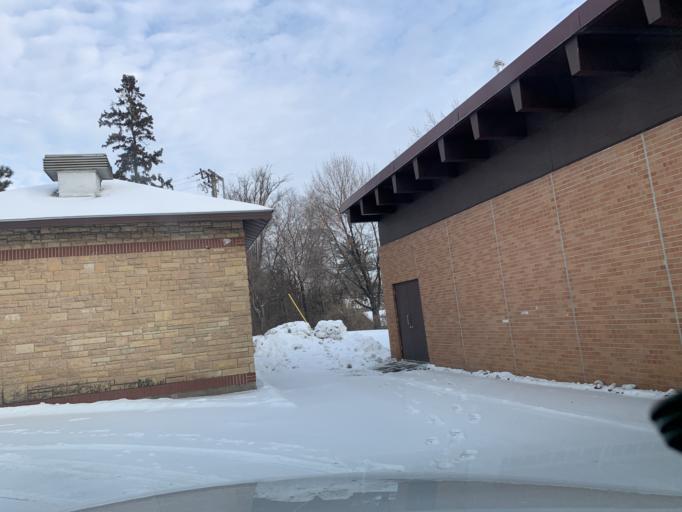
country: US
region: Minnesota
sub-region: Hennepin County
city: Saint Louis Park
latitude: 44.9229
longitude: -93.3538
